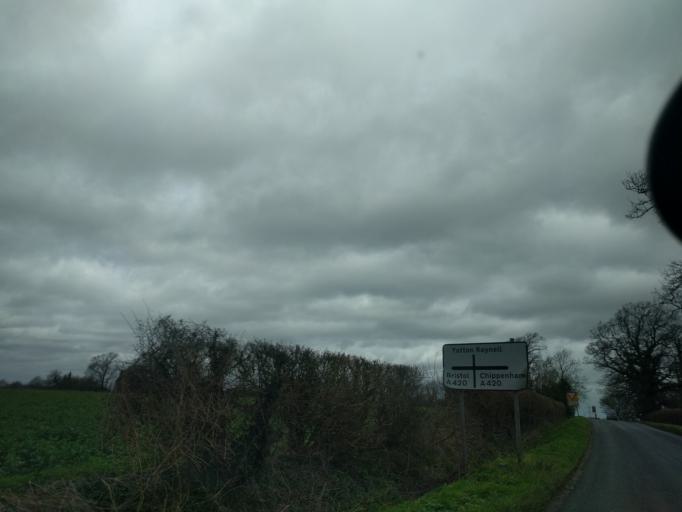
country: GB
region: England
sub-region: Wiltshire
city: Biddestone
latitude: 51.4701
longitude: -2.1954
